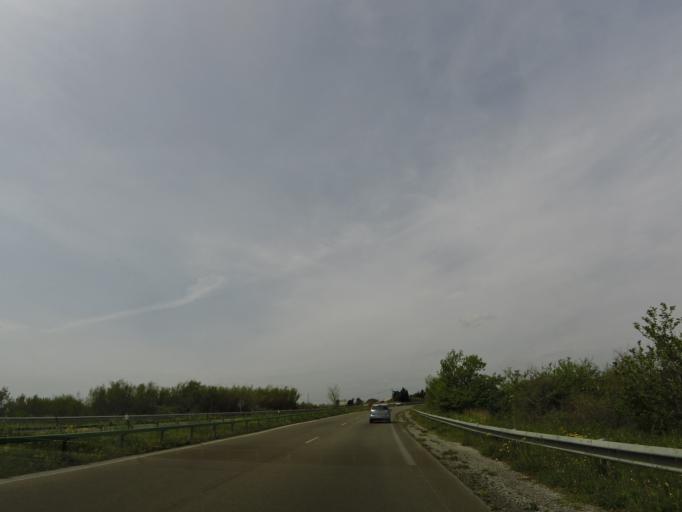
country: FR
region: Languedoc-Roussillon
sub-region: Departement de l'Herault
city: Perols
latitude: 43.5512
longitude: 3.9729
